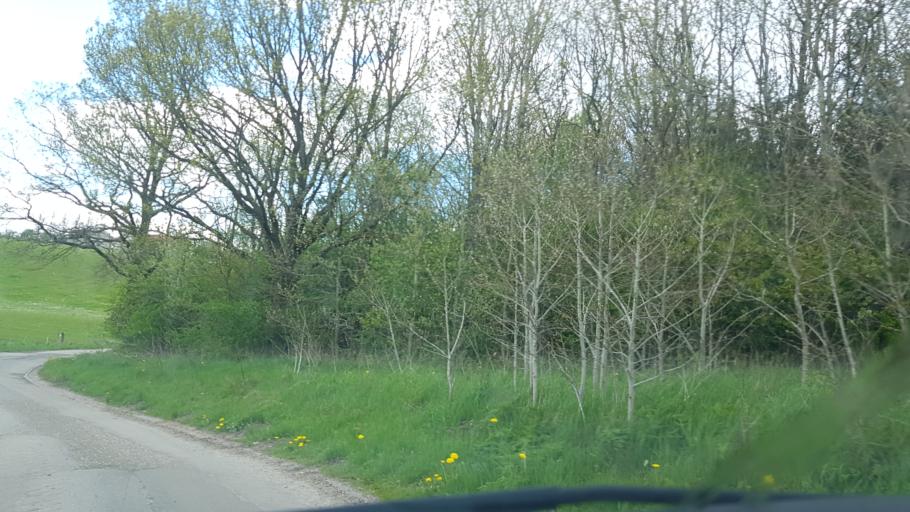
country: DK
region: South Denmark
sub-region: Haderslev Kommune
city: Vojens
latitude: 55.2428
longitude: 9.3378
